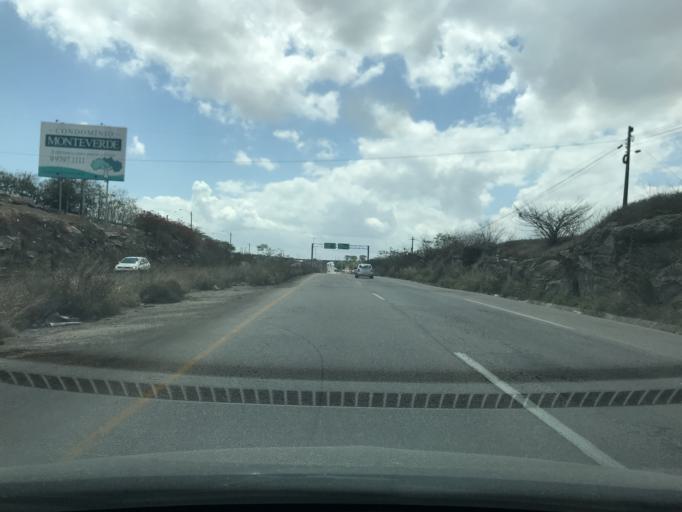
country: BR
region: Pernambuco
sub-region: Caruaru
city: Caruaru
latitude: -8.3077
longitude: -35.9570
